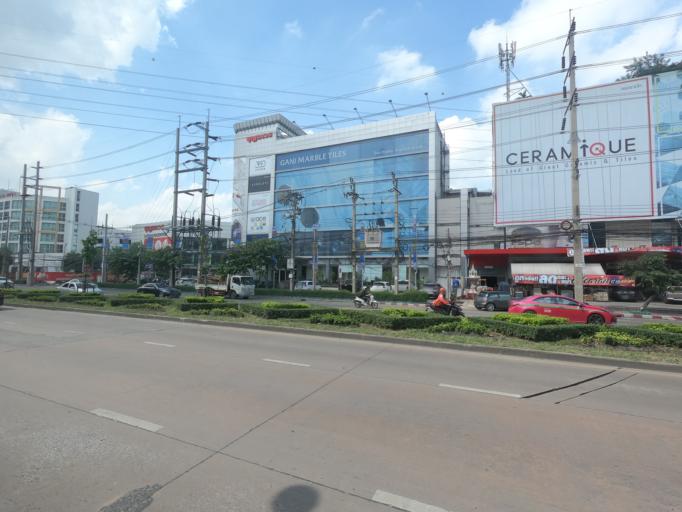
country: TH
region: Bangkok
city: Huai Khwang
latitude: 13.7942
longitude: 100.5743
